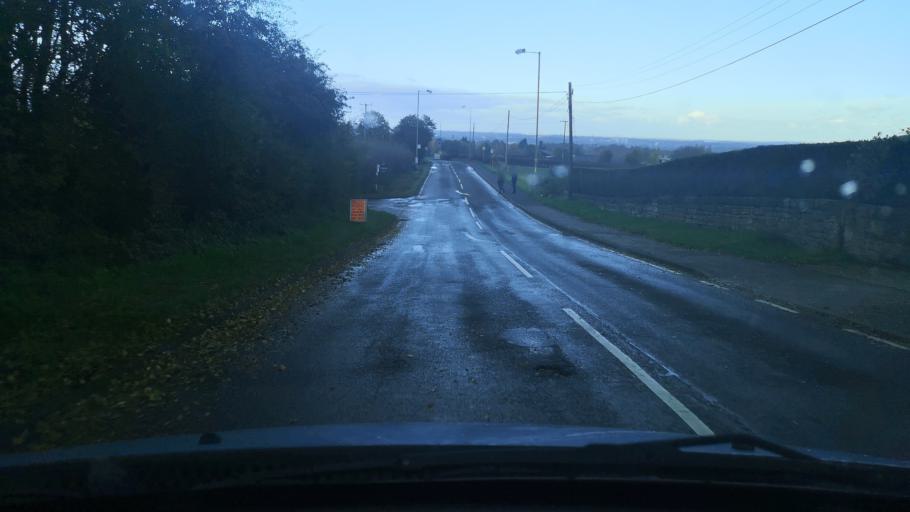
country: GB
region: England
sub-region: City and Borough of Wakefield
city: Woolley
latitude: 53.6260
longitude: -1.5245
